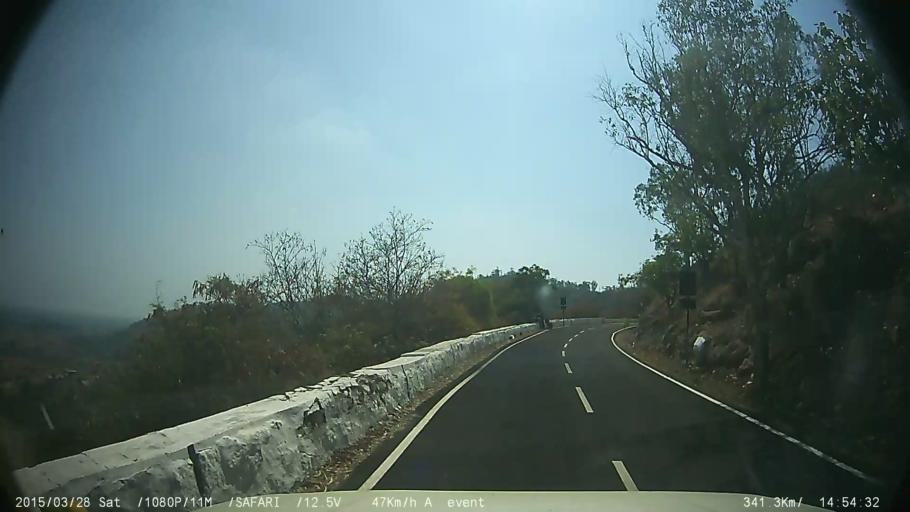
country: IN
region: Karnataka
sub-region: Mysore
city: Mysore
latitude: 12.2823
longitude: 76.6940
